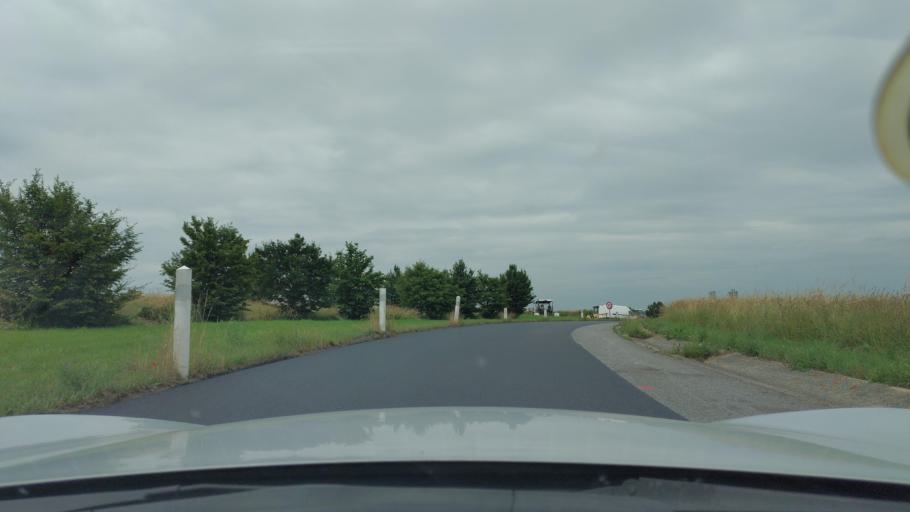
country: FR
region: Picardie
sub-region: Departement de l'Oise
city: Margny-les-Compiegne
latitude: 49.4389
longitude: 2.8212
